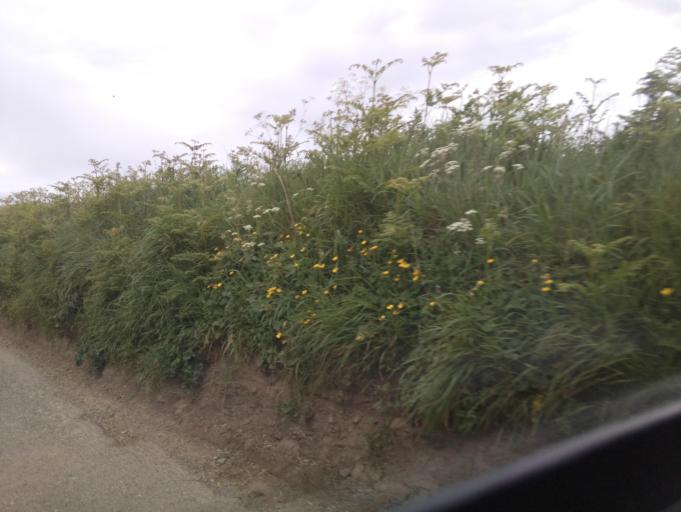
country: GB
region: England
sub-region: Devon
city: Dartmouth
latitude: 50.3436
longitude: -3.6546
